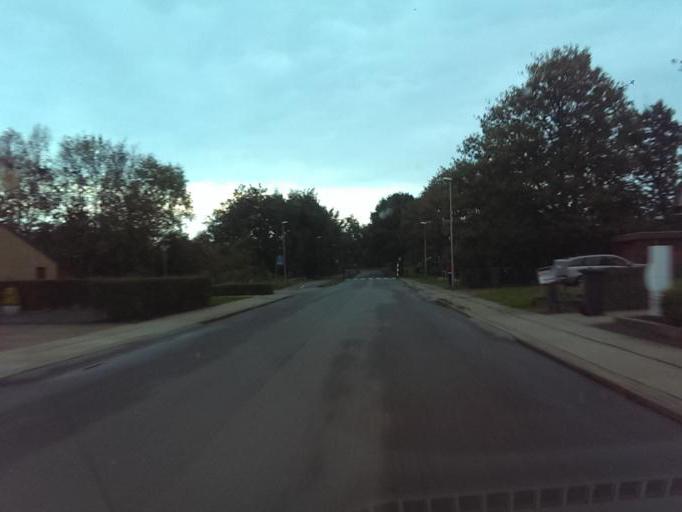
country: DK
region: South Denmark
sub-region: Esbjerg Kommune
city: Bramming
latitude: 55.4704
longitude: 8.7121
